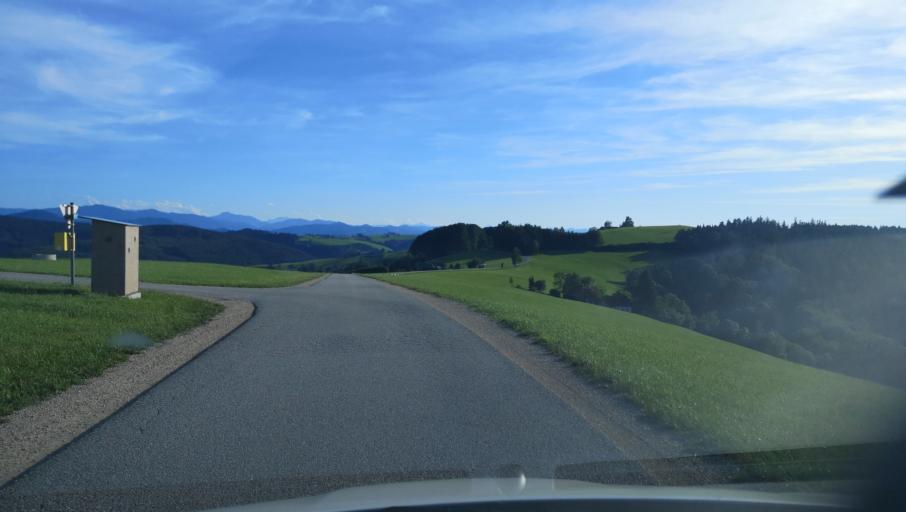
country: AT
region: Lower Austria
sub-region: Politischer Bezirk Amstetten
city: Euratsfeld
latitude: 48.0243
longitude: 14.9105
